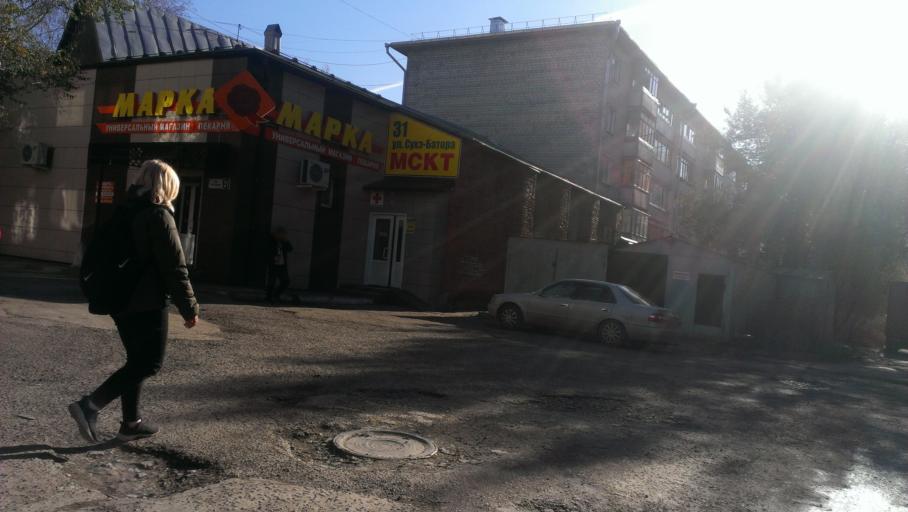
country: RU
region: Altai Krai
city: Novosilikatnyy
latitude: 53.3507
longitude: 83.6804
